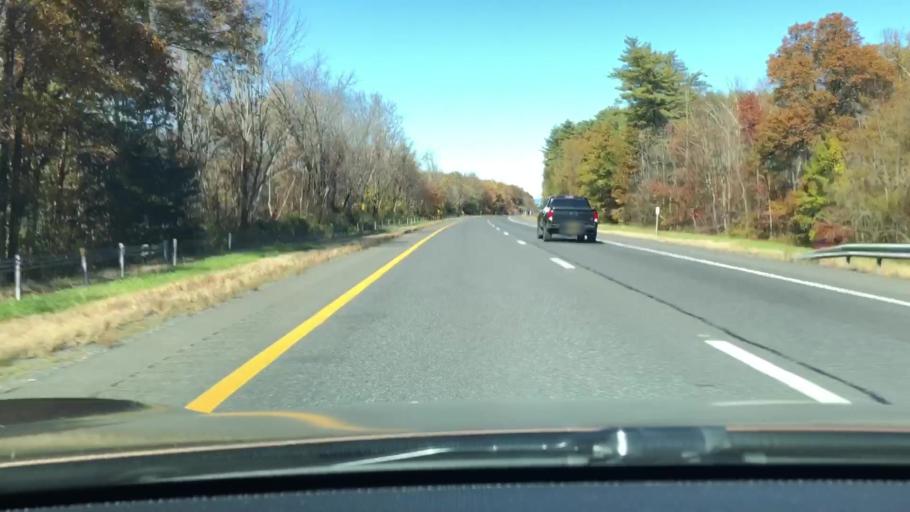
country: US
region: New York
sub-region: Ulster County
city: Tillson
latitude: 41.7927
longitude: -74.0510
